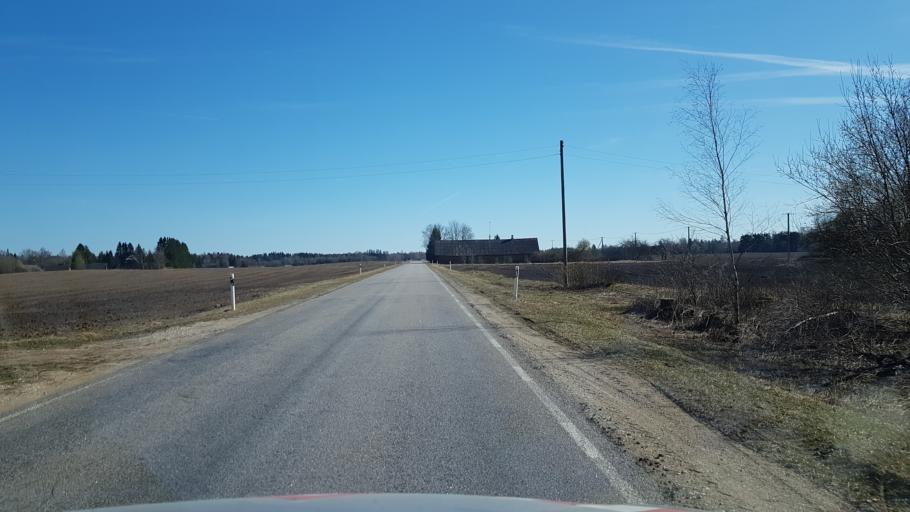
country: EE
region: Laeaene-Virumaa
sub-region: Vinni vald
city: Vinni
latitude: 59.2448
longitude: 26.6899
